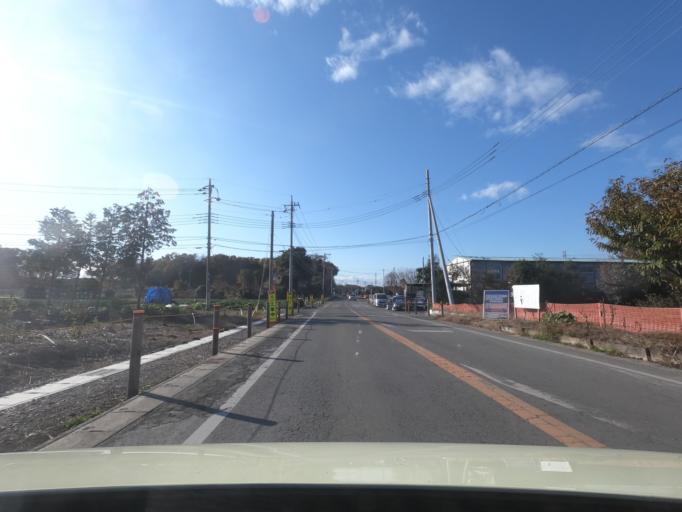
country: JP
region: Ibaraki
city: Koga
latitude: 36.2368
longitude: 139.7576
